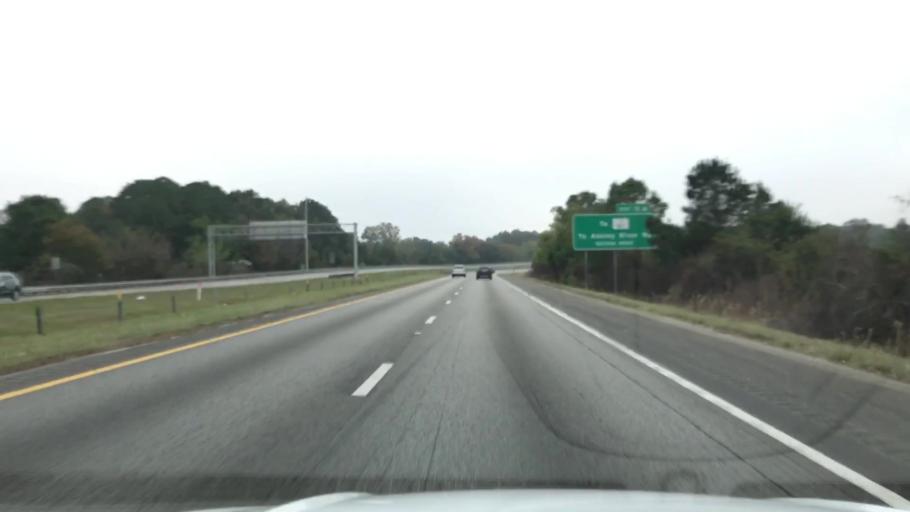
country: US
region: South Carolina
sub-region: Charleston County
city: North Charleston
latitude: 32.8213
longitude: -80.0308
